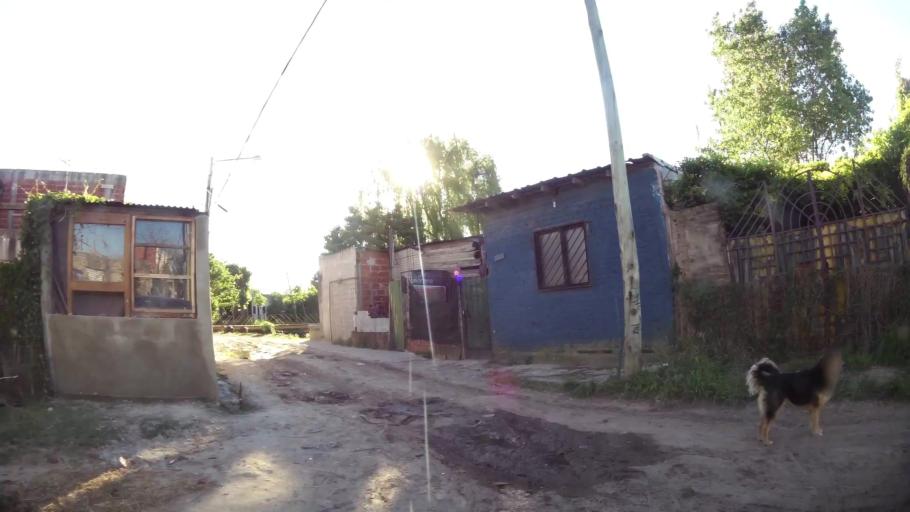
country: AR
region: Buenos Aires
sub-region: Partido de Almirante Brown
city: Adrogue
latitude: -34.7692
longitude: -58.3274
